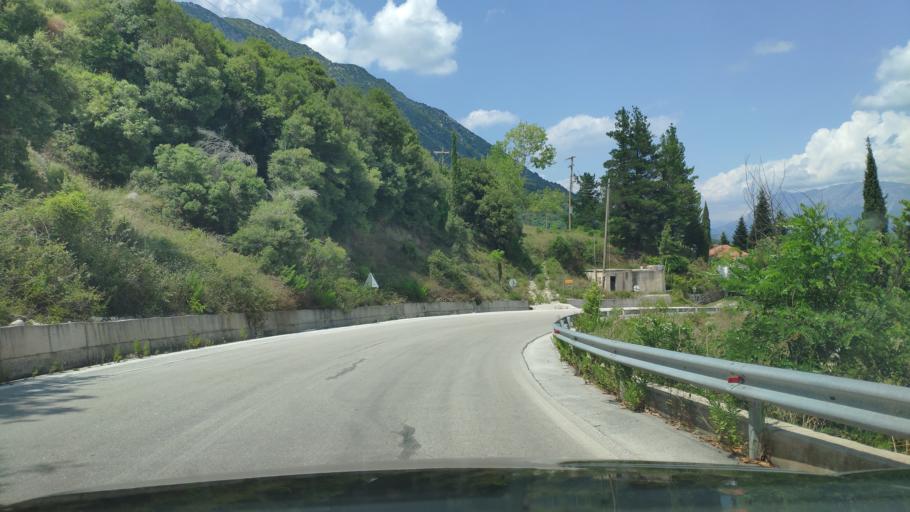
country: GR
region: Epirus
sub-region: Nomos Artas
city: Agios Dimitrios
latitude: 39.3402
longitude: 21.0064
